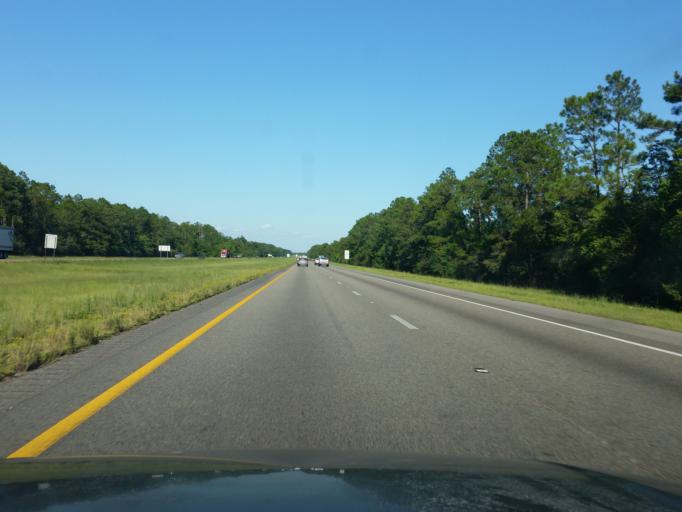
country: US
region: Mississippi
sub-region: Hancock County
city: Diamondhead
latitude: 30.3754
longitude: -89.3674
